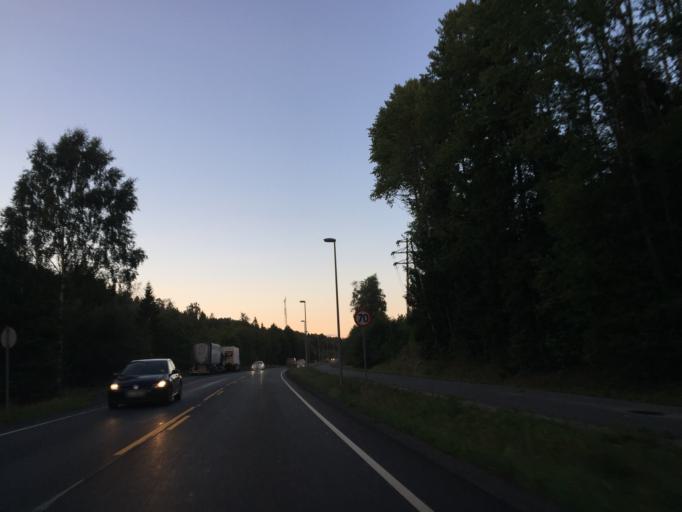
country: NO
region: Ostfold
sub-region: Moss
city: Moss
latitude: 59.4574
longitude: 10.6872
